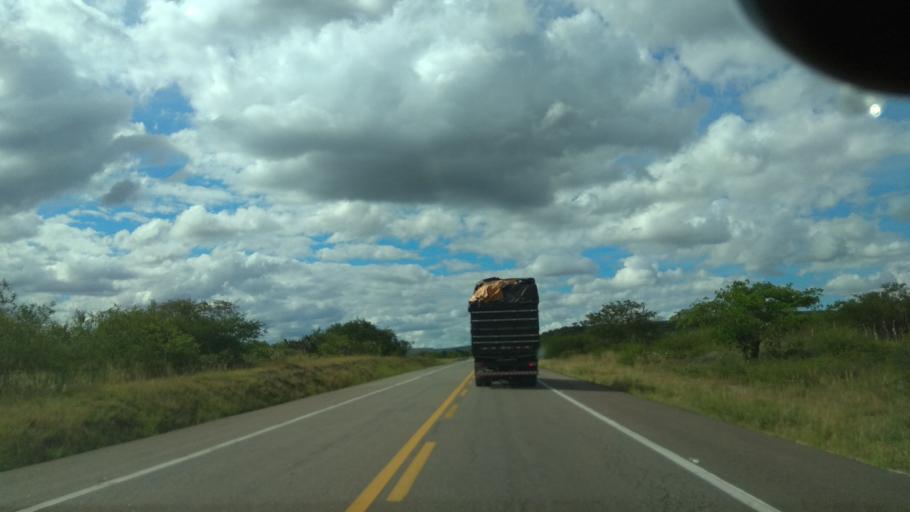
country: BR
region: Bahia
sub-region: Amargosa
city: Amargosa
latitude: -12.9452
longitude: -39.9132
